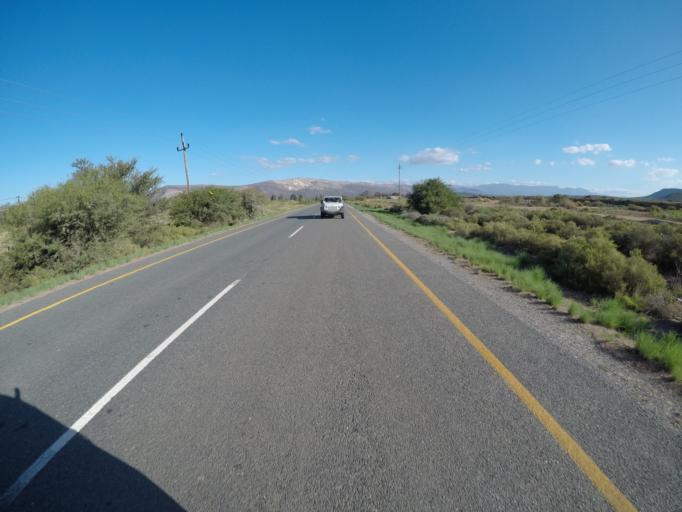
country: ZA
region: Western Cape
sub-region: Cape Winelands District Municipality
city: Ashton
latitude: -33.8028
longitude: 19.7817
